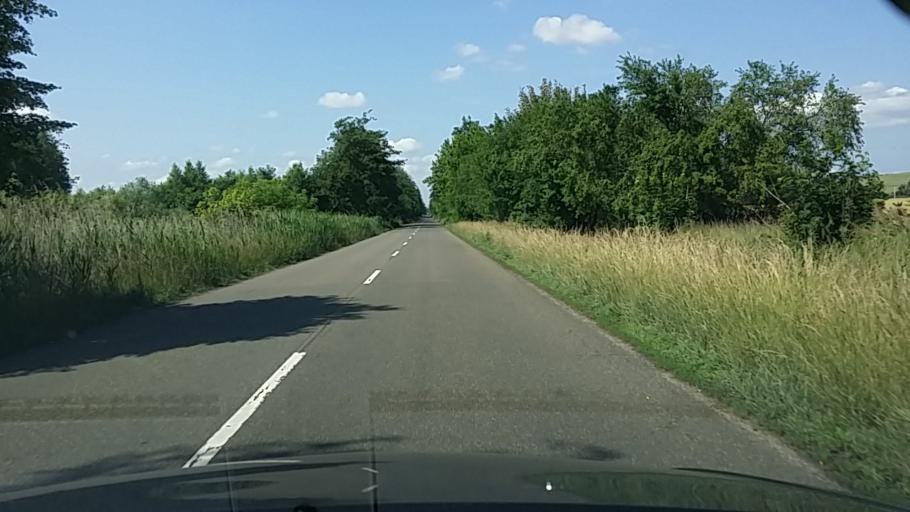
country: HU
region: Komarom-Esztergom
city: Esztergom
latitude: 47.8964
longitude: 18.7755
